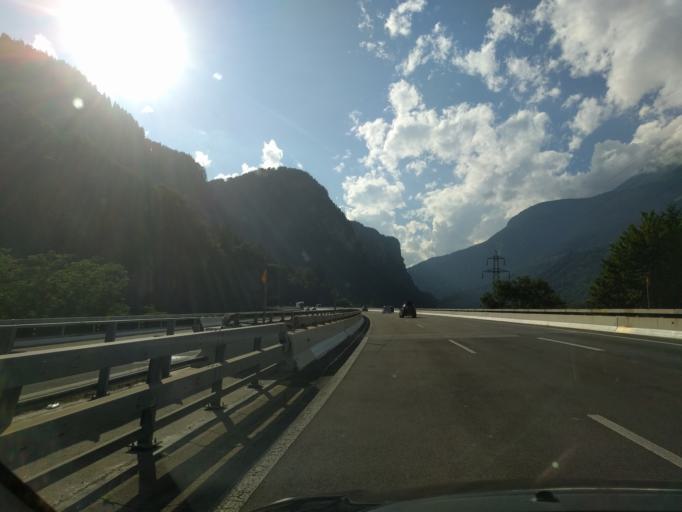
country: CH
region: Ticino
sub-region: Leventina District
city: Faido
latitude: 46.4736
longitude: 8.8061
